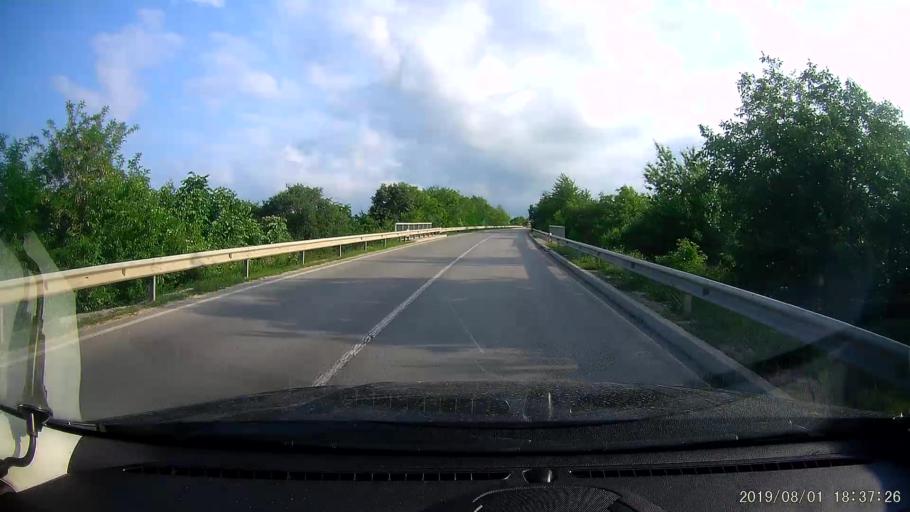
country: BG
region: Shumen
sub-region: Obshtina Khitrino
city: Gara Khitrino
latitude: 43.4211
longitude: 26.9304
